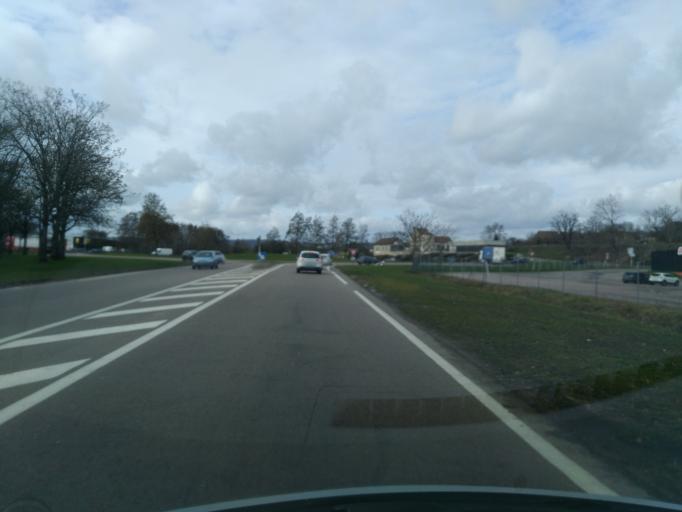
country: FR
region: Bourgogne
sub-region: Departement de Saone-et-Loire
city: Torcy
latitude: 46.7671
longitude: 4.4537
